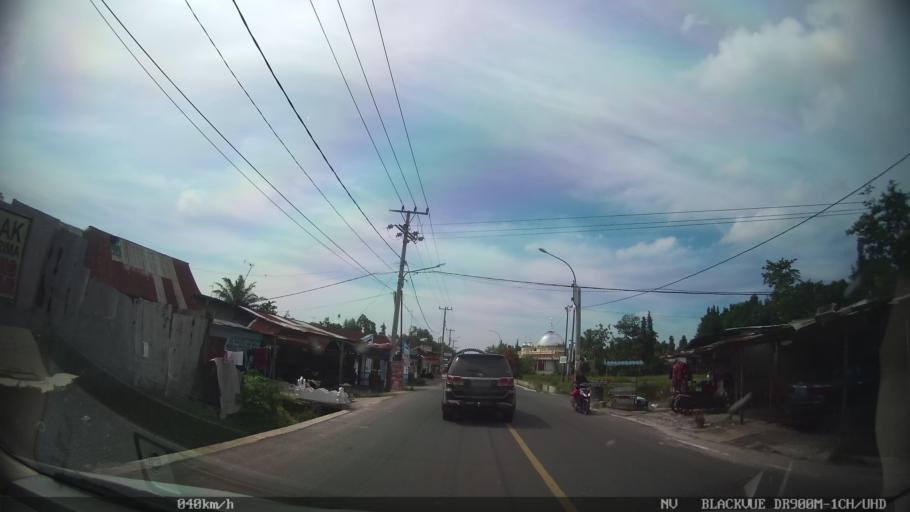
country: ID
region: North Sumatra
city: Percut
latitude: 3.6007
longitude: 98.8585
